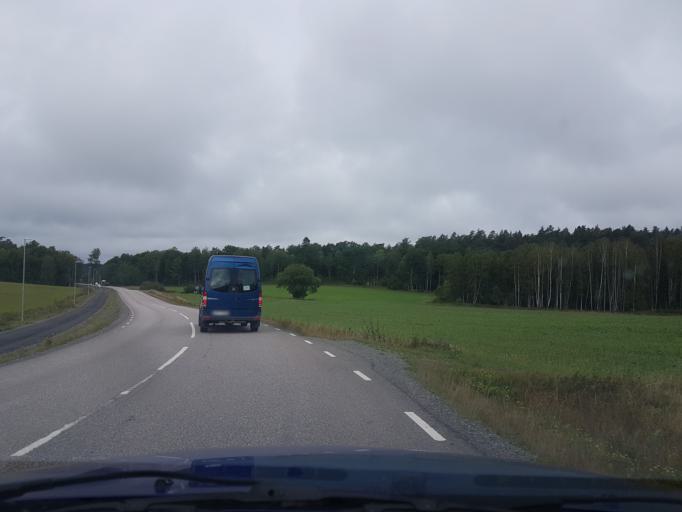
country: SE
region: Vaestra Goetaland
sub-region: Ale Kommun
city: Alvangen
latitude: 57.9386
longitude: 12.1558
